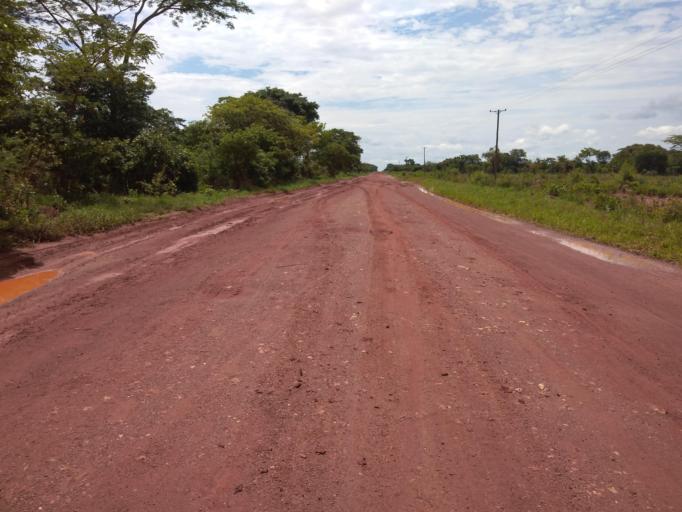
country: ZM
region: Copperbelt
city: Luanshya
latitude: -13.4833
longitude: 28.7108
